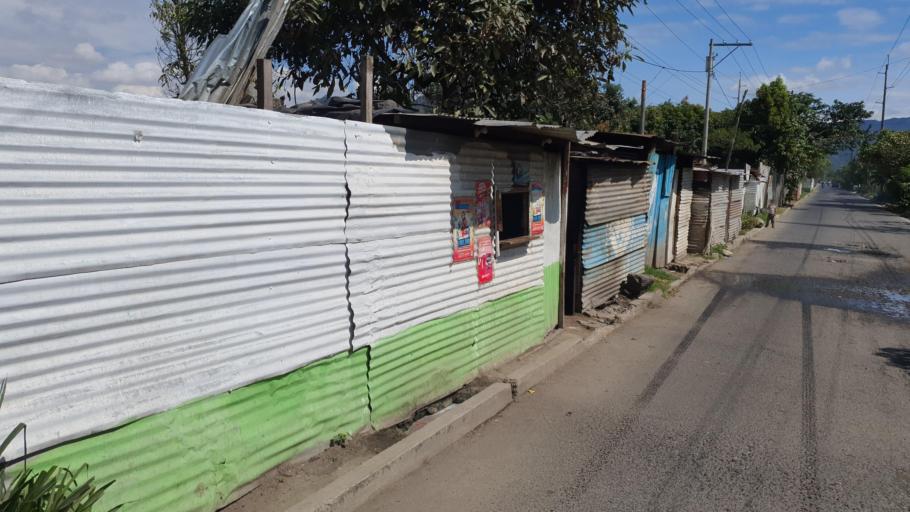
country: GT
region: Guatemala
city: Villa Canales
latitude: 14.4591
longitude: -90.5569
